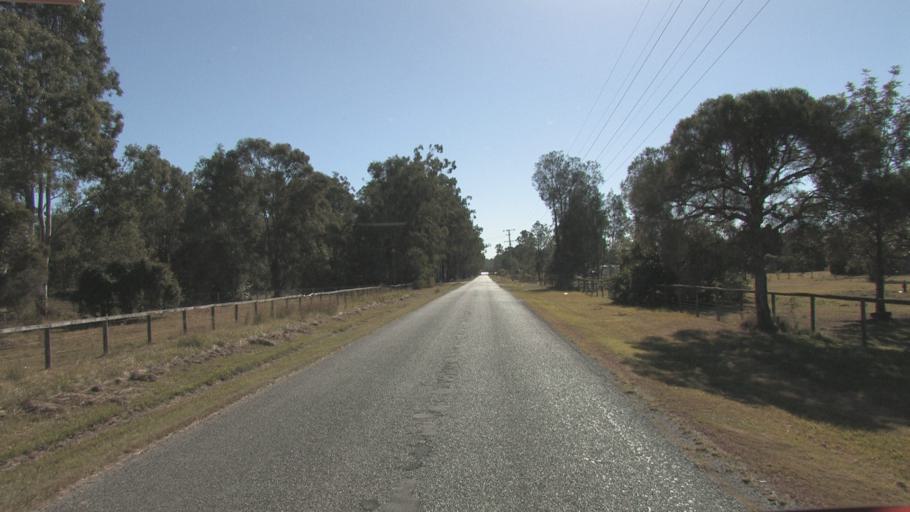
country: AU
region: Queensland
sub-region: Logan
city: Chambers Flat
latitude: -27.7558
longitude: 153.0758
